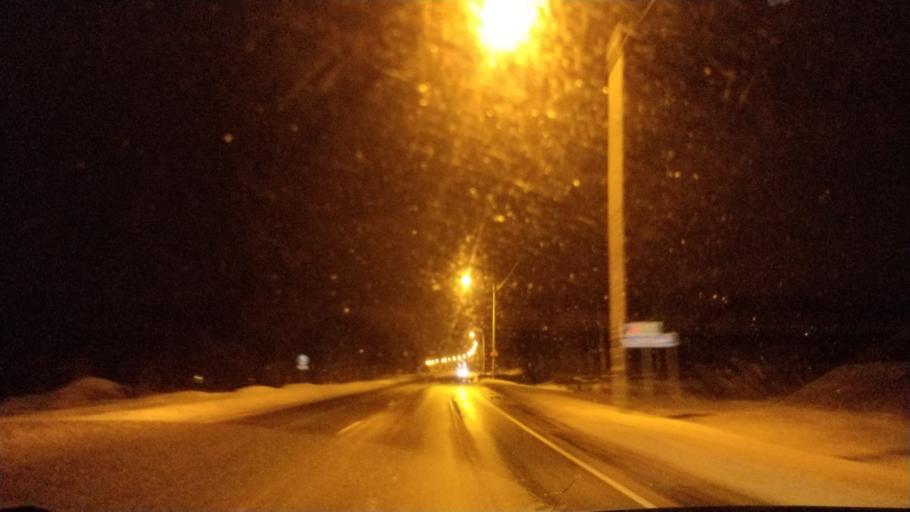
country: FI
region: Lapland
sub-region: Kemi-Tornio
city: Tervola
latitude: 66.1435
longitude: 24.9567
